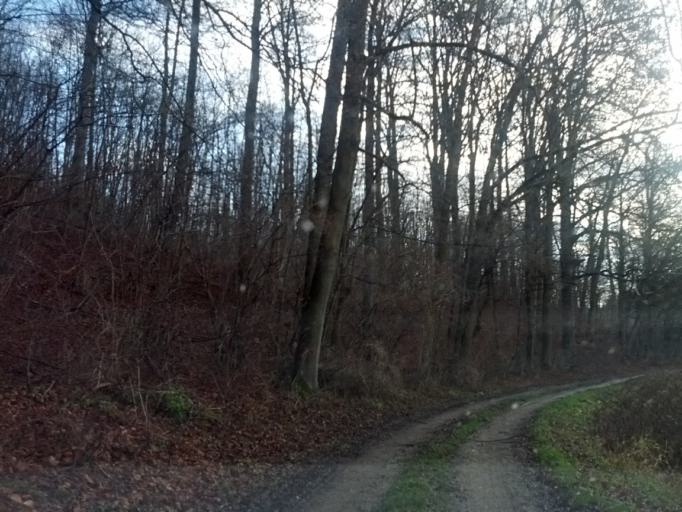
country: DE
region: Thuringia
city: Wolfsburg-Unkeroda
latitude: 50.9663
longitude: 10.2266
